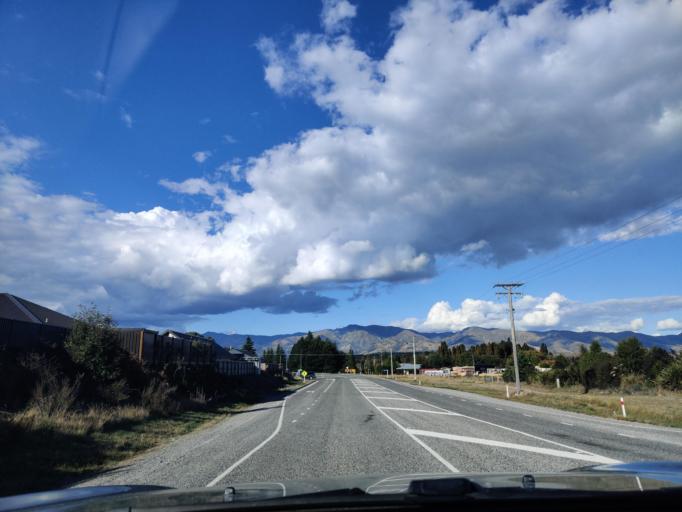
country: NZ
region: Otago
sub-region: Queenstown-Lakes District
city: Wanaka
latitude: -44.6842
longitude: 169.1874
